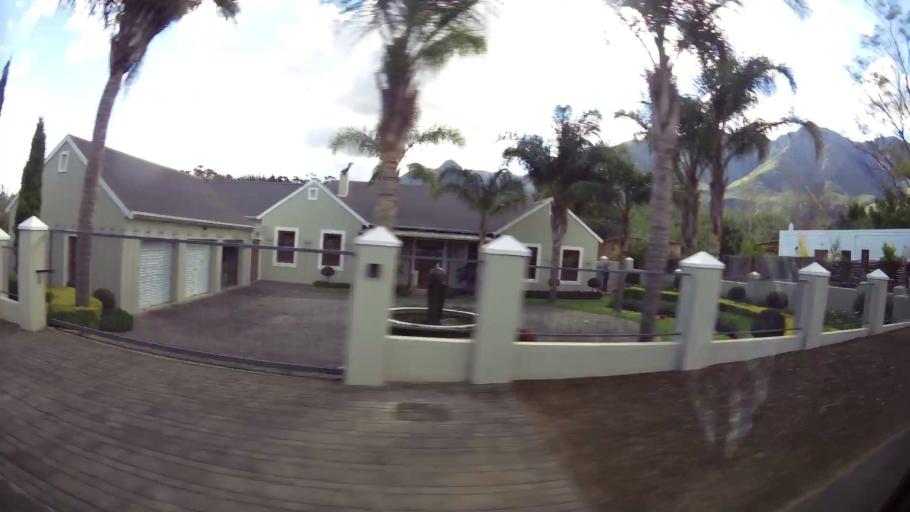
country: ZA
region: Western Cape
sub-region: Overberg District Municipality
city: Swellendam
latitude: -34.0125
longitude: 20.4573
